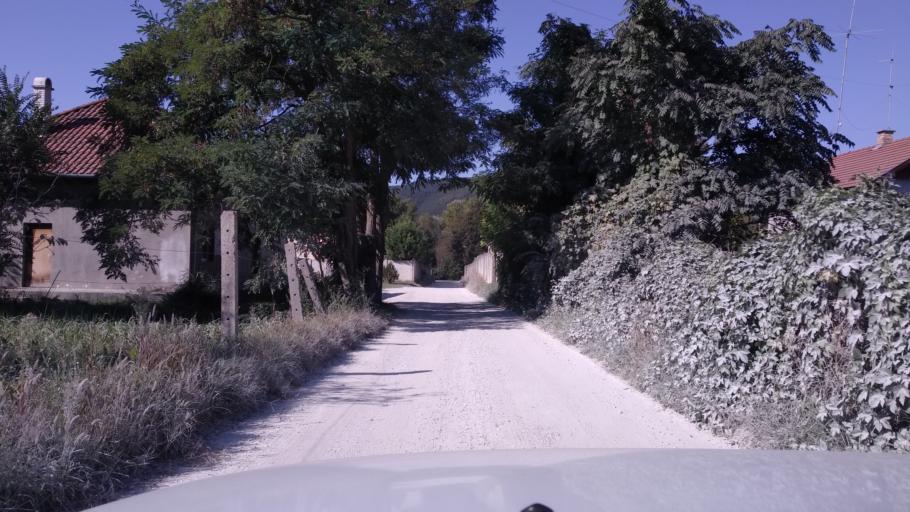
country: HU
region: Komarom-Esztergom
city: Esztergom
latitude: 47.8131
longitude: 18.7860
